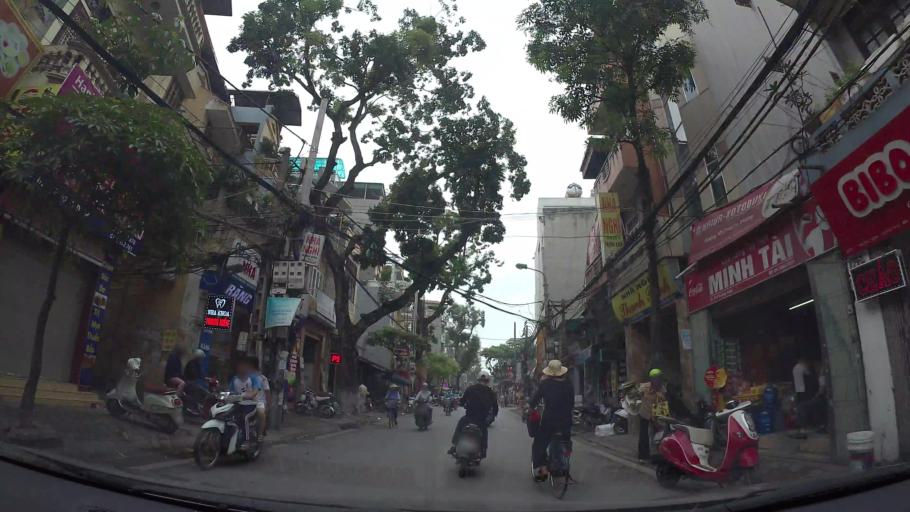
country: VN
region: Ha Noi
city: Van Dien
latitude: 20.9781
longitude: 105.8424
